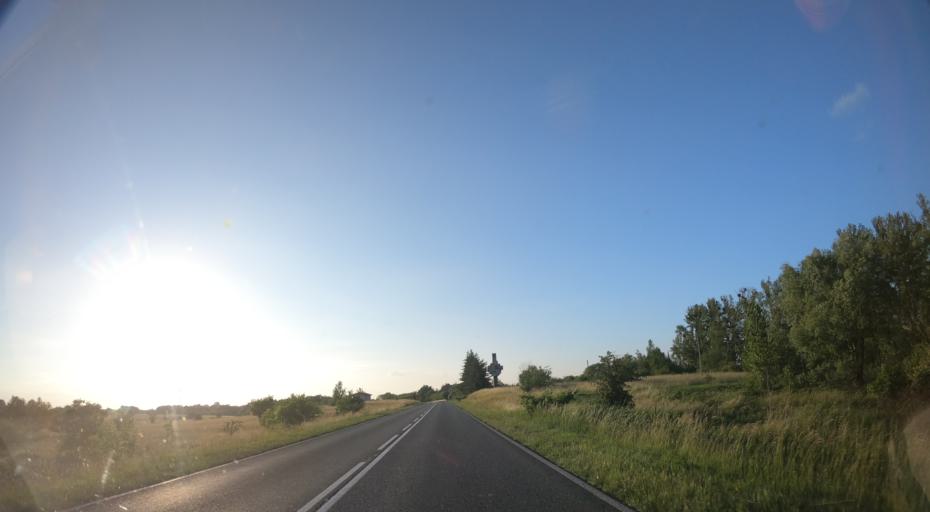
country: PL
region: West Pomeranian Voivodeship
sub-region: Powiat pyrzycki
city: Lipiany
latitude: 52.9973
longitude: 14.9679
